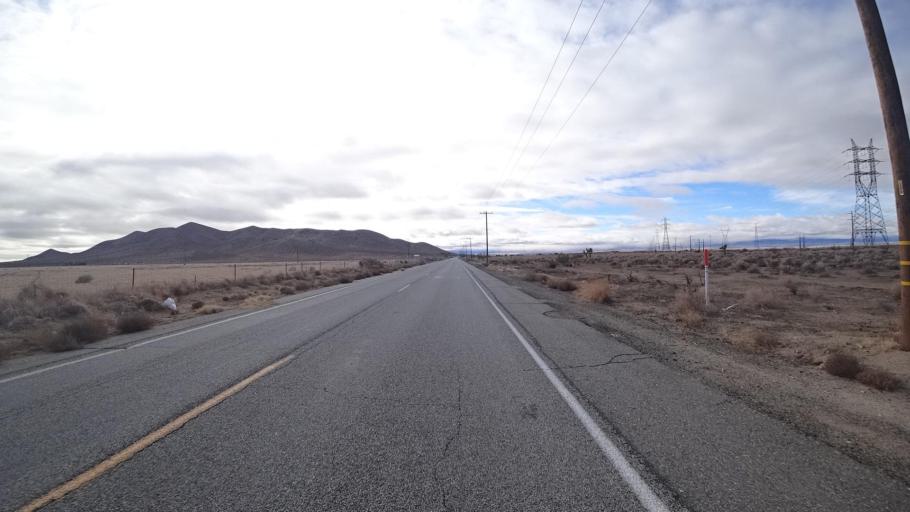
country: US
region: California
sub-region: Kern County
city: Rosamond
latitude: 34.8985
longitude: -118.2913
